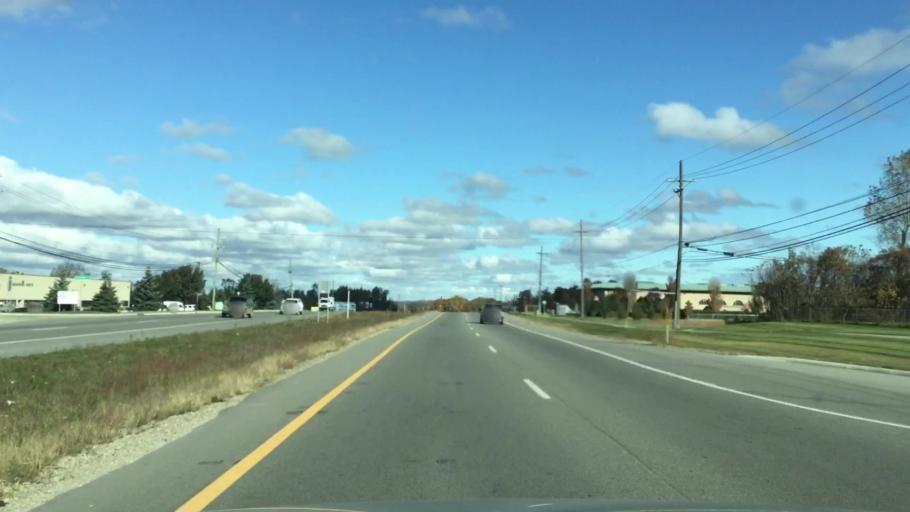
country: US
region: Michigan
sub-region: Oakland County
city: Auburn Hills
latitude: 42.7167
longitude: -83.2426
